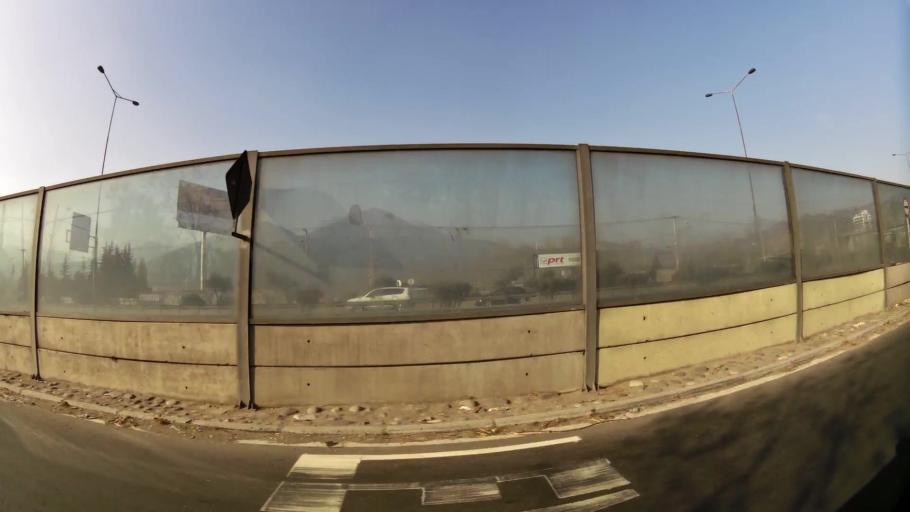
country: CL
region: Santiago Metropolitan
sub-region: Provincia de Santiago
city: Santiago
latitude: -33.3914
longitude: -70.6298
